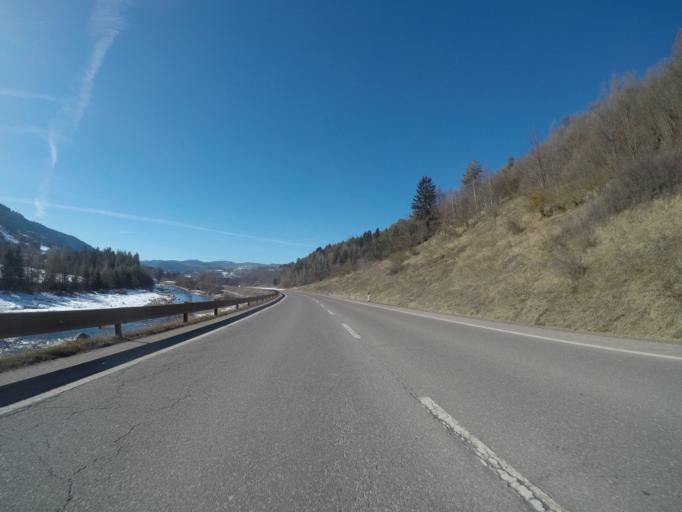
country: IT
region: Trentino-Alto Adige
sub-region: Provincia di Trento
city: Tesero
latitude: 46.2866
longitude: 11.5037
